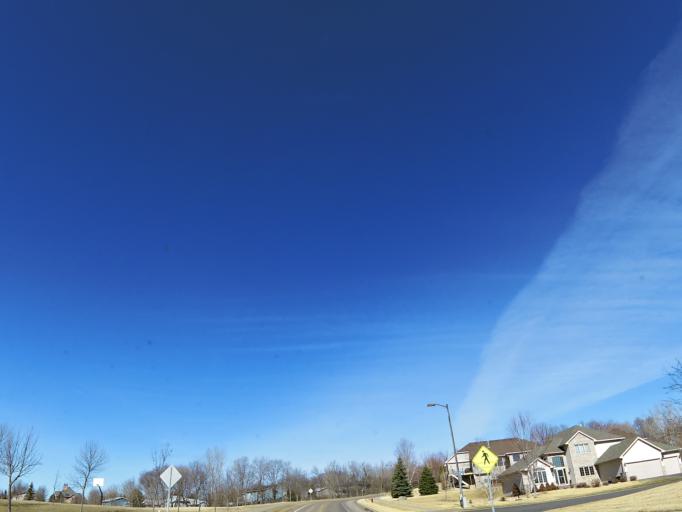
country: US
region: Minnesota
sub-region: Scott County
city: Prior Lake
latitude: 44.7291
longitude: -93.4573
